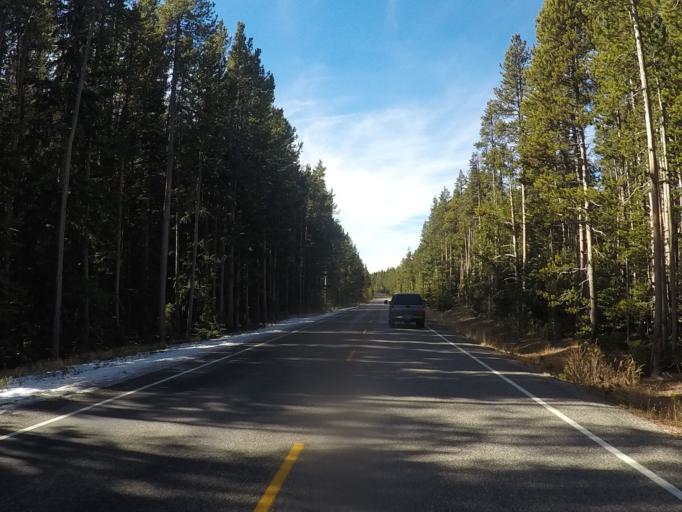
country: US
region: Montana
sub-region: Gallatin County
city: West Yellowstone
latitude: 44.4586
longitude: -110.4857
